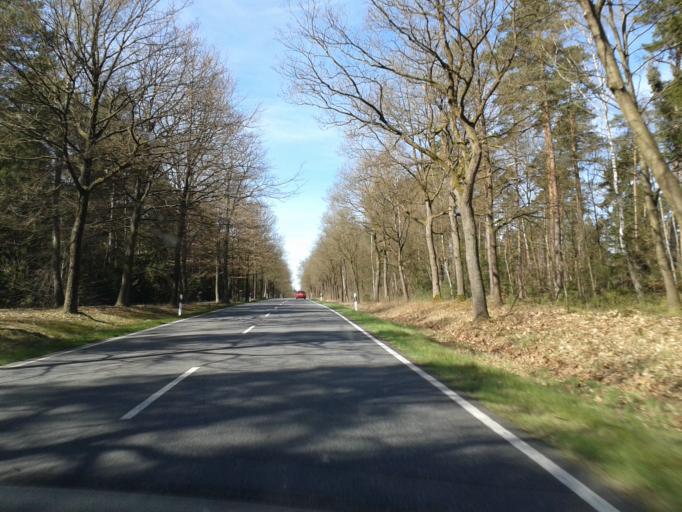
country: DE
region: Lower Saxony
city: Fassberg
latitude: 52.9561
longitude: 10.1750
